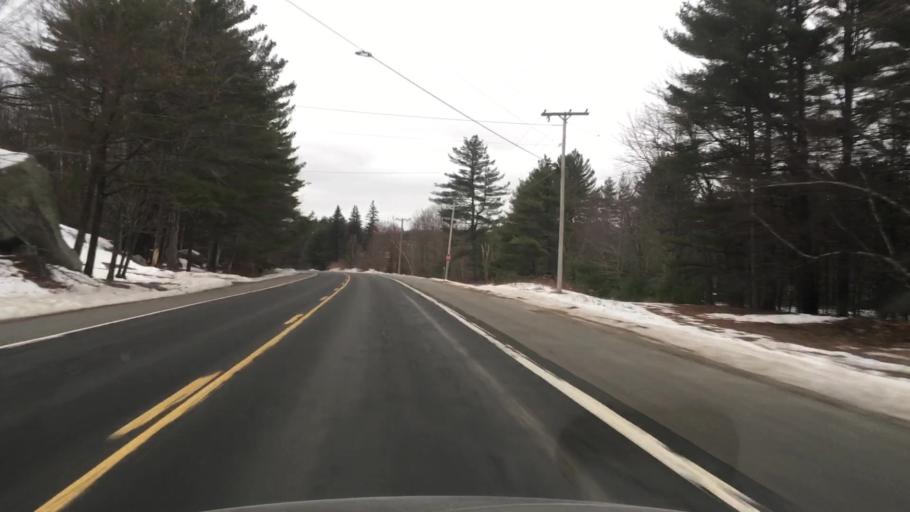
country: US
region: New Hampshire
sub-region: Merrimack County
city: Henniker
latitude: 43.2219
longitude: -71.8825
